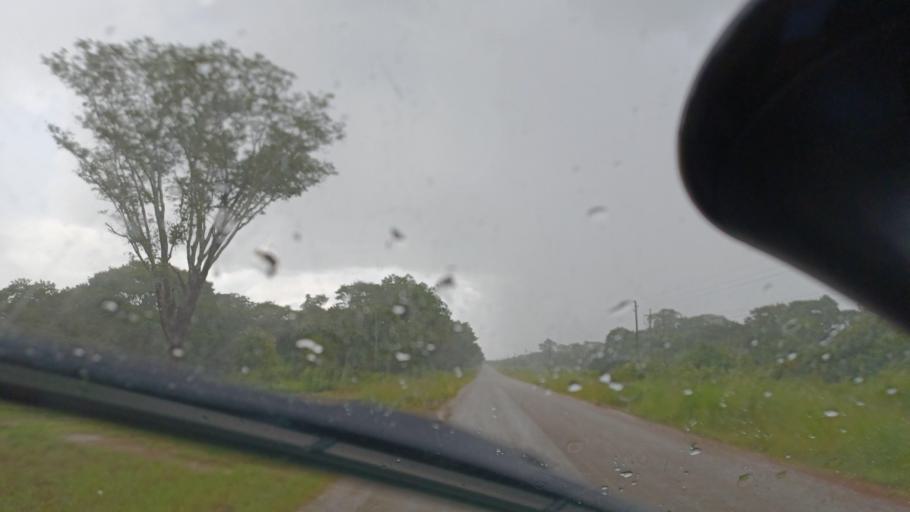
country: ZM
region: North-Western
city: Kasempa
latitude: -13.0909
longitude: 25.9416
